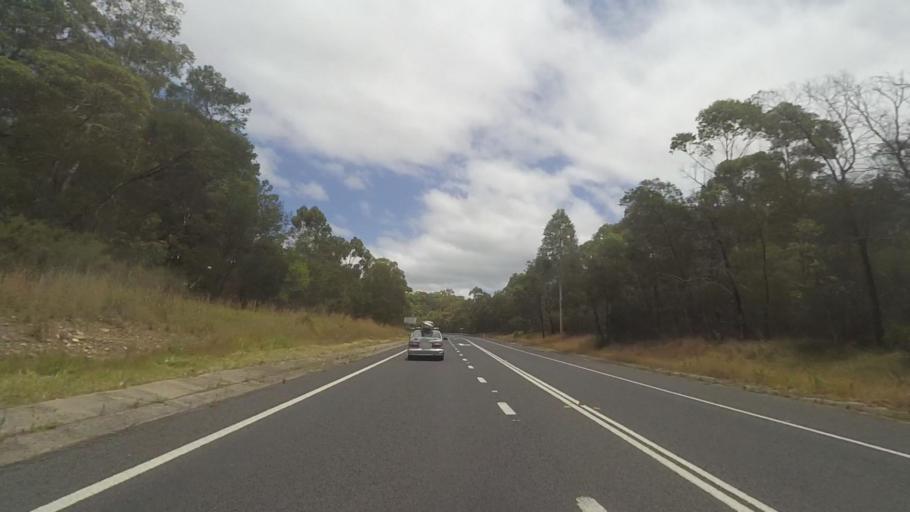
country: AU
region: New South Wales
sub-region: Shoalhaven Shire
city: Milton
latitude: -35.2407
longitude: 150.4285
